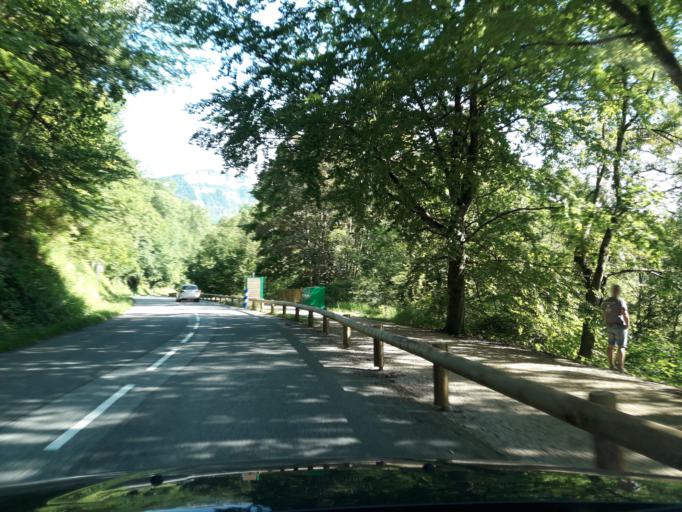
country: FR
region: Rhone-Alpes
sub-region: Departement de la Savoie
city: Vimines
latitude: 45.5623
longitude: 5.8121
